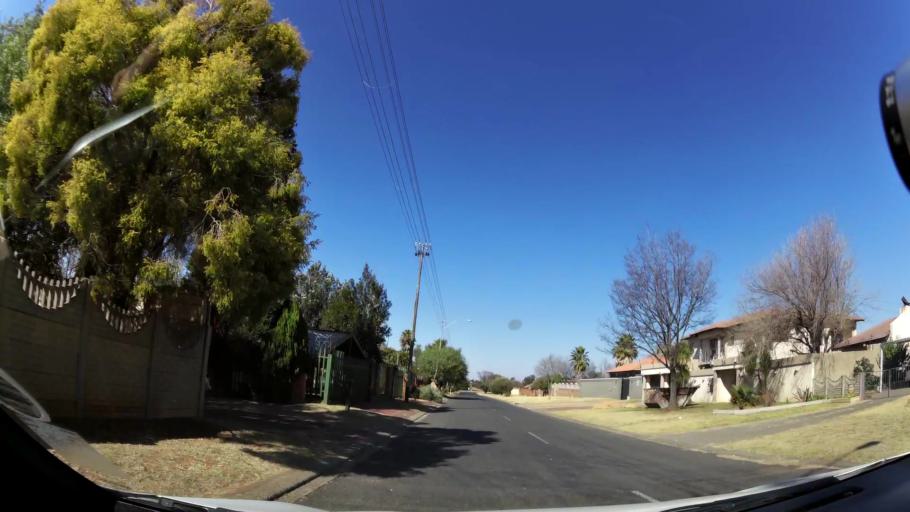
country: ZA
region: Gauteng
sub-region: City of Johannesburg Metropolitan Municipality
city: Johannesburg
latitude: -26.2687
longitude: 28.0294
